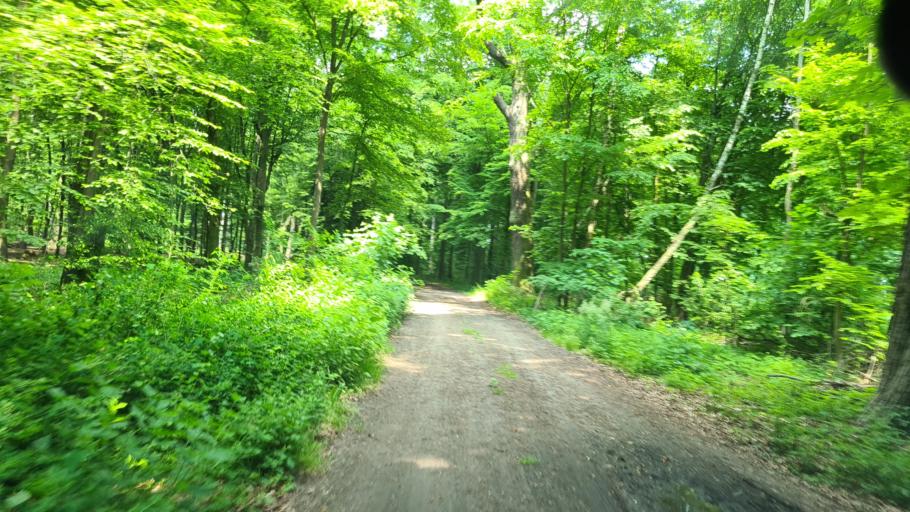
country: DE
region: Brandenburg
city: Sonnewalde
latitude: 51.7014
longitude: 13.6381
